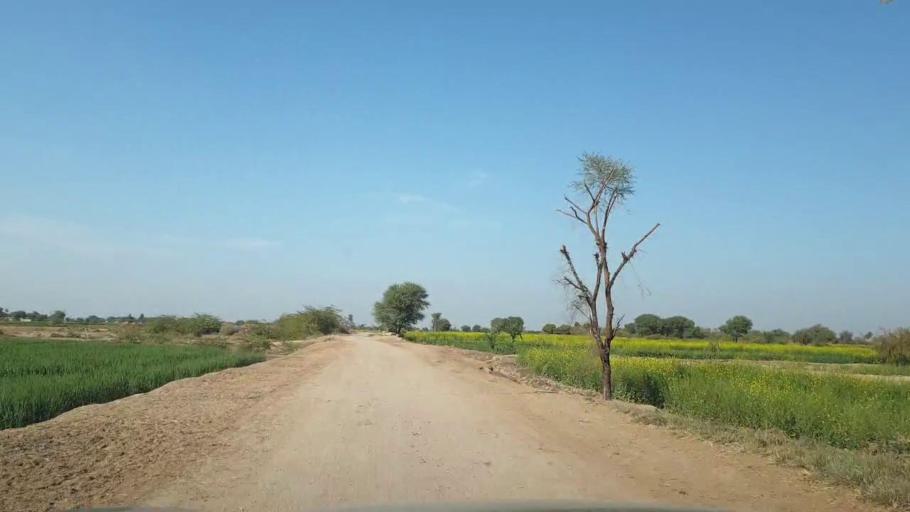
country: PK
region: Sindh
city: Tando Adam
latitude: 25.6726
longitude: 68.6862
